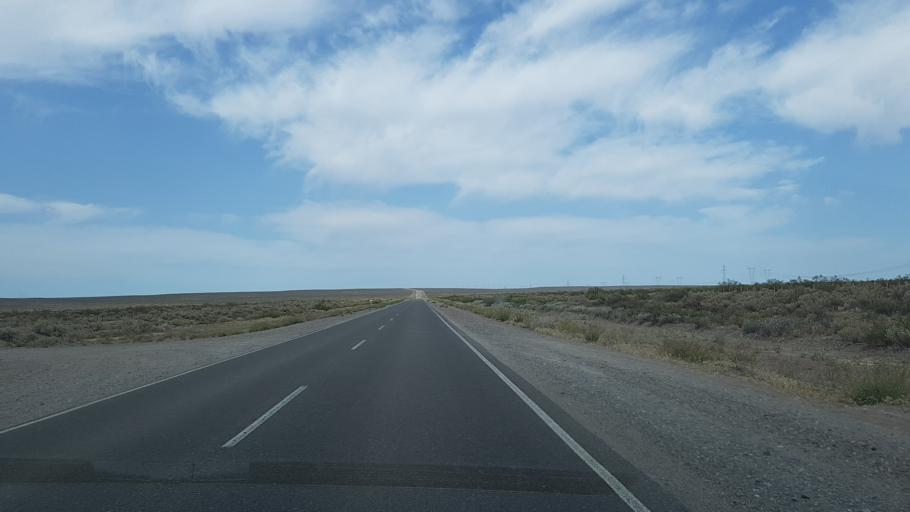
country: AR
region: Neuquen
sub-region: Departamento de Picun Leufu
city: Picun Leufu
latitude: -39.7171
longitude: -69.5314
